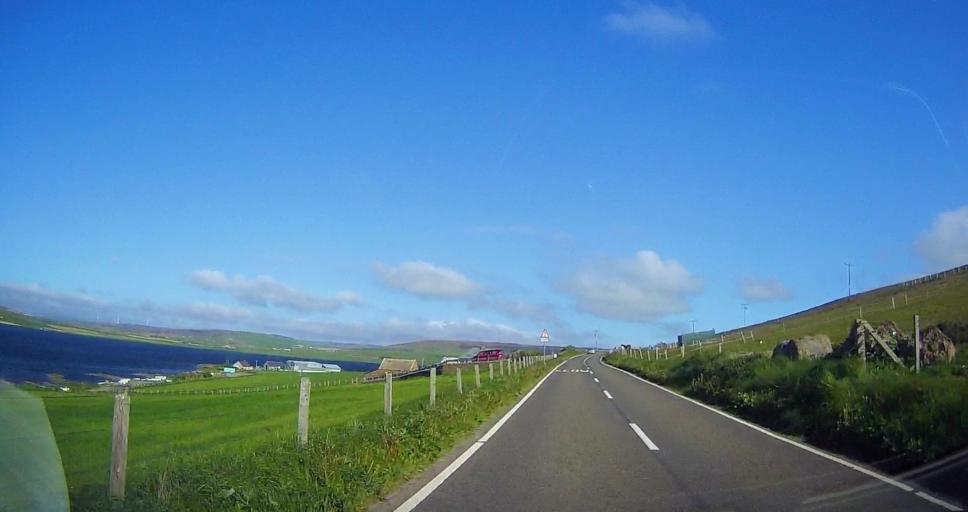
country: GB
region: Scotland
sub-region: Orkney Islands
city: Stromness
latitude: 59.1101
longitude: -3.2872
